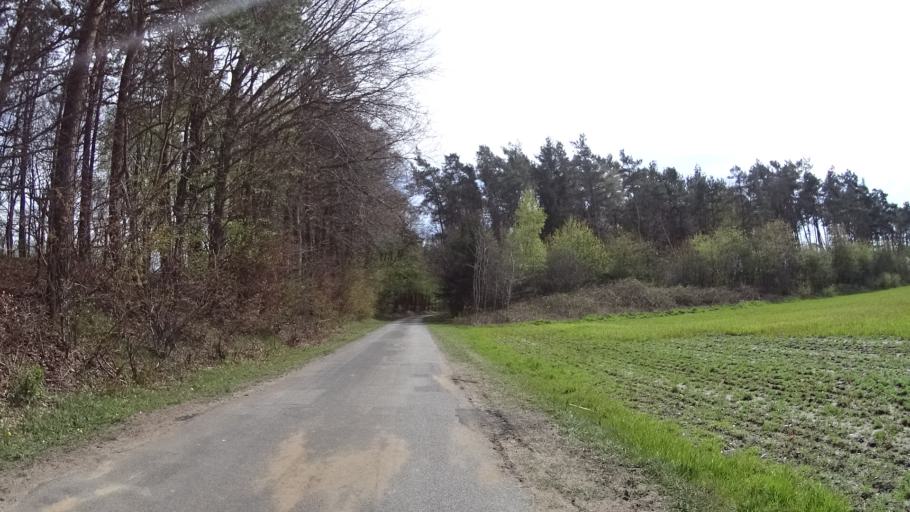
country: DE
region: Lower Saxony
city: Lunne
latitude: 52.3874
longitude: 7.3920
